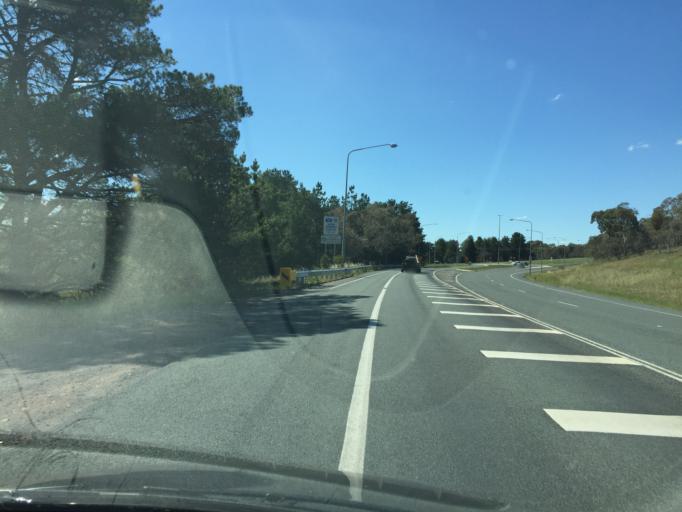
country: AU
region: Australian Capital Territory
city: Macarthur
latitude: -35.4385
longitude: 149.1265
